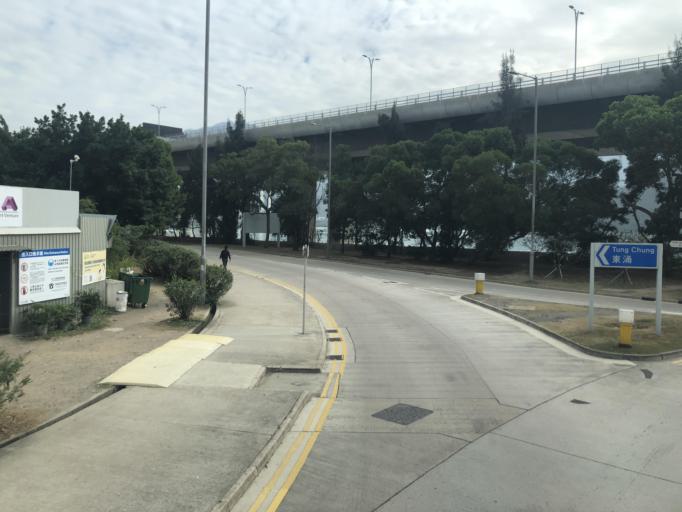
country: HK
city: Tai O
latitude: 22.2934
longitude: 113.9256
